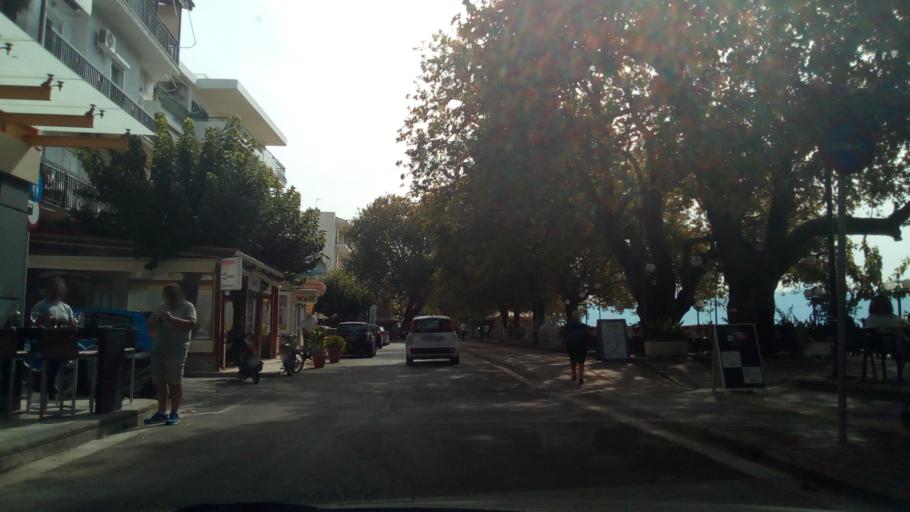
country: GR
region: West Greece
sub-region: Nomos Aitolias kai Akarnanias
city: Nafpaktos
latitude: 38.3921
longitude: 21.8365
